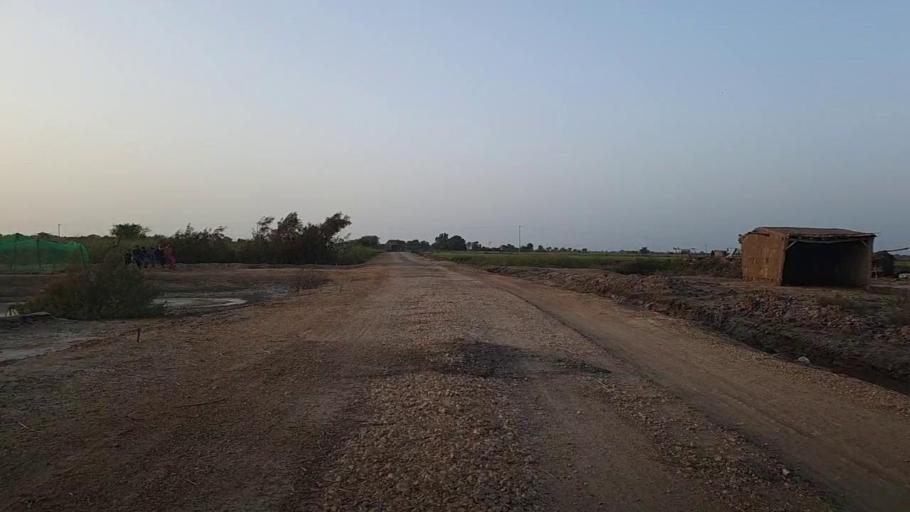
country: PK
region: Sindh
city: Kario
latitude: 24.7283
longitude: 68.4608
